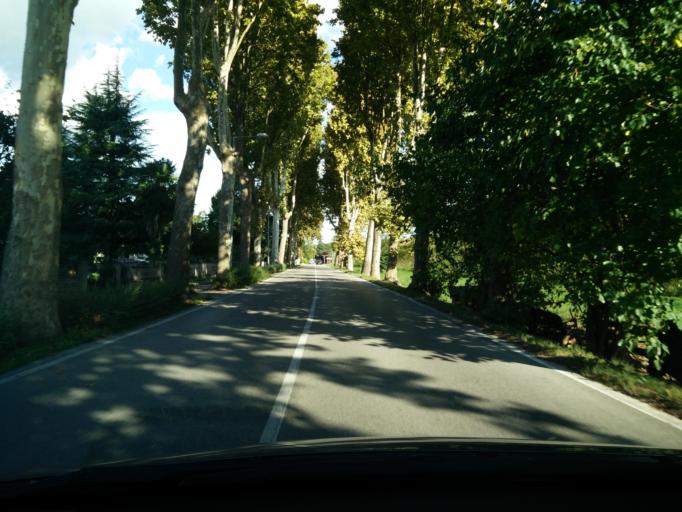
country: IT
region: Veneto
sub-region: Provincia di Venezia
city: Noventa di Piave
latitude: 45.6694
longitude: 12.5128
